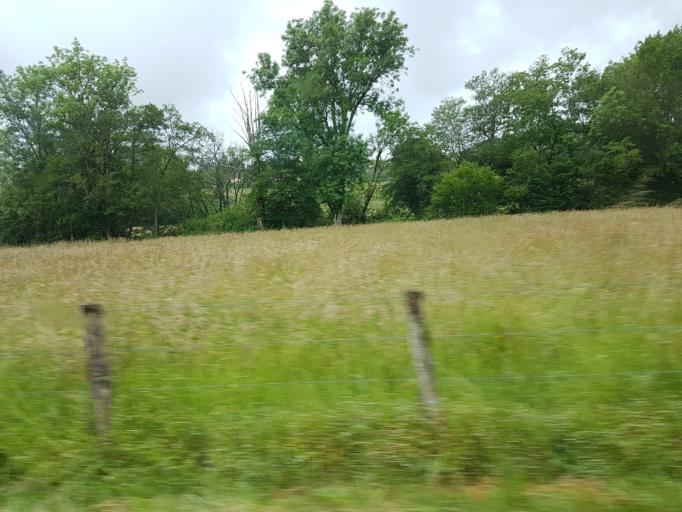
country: FR
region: Bourgogne
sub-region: Departement de la Nievre
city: Lormes
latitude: 47.1702
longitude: 3.8382
